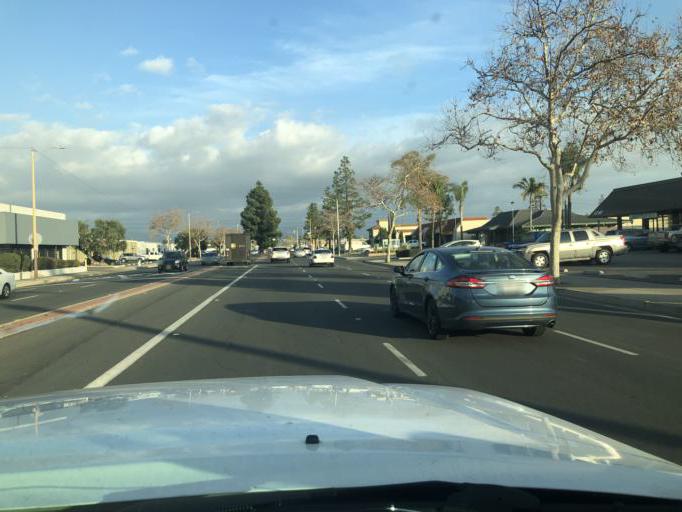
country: US
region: California
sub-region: Orange County
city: Santa Ana
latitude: 33.7268
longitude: -117.8536
